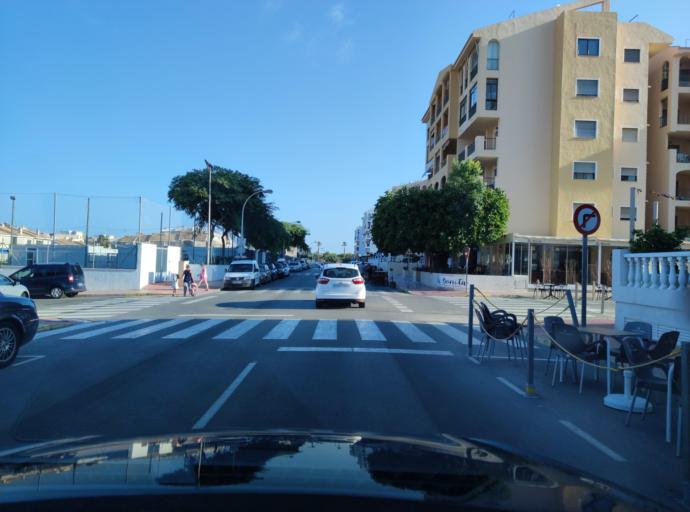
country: ES
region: Valencia
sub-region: Provincia de Alicante
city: Guardamar del Segura
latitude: 38.0824
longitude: -0.6515
